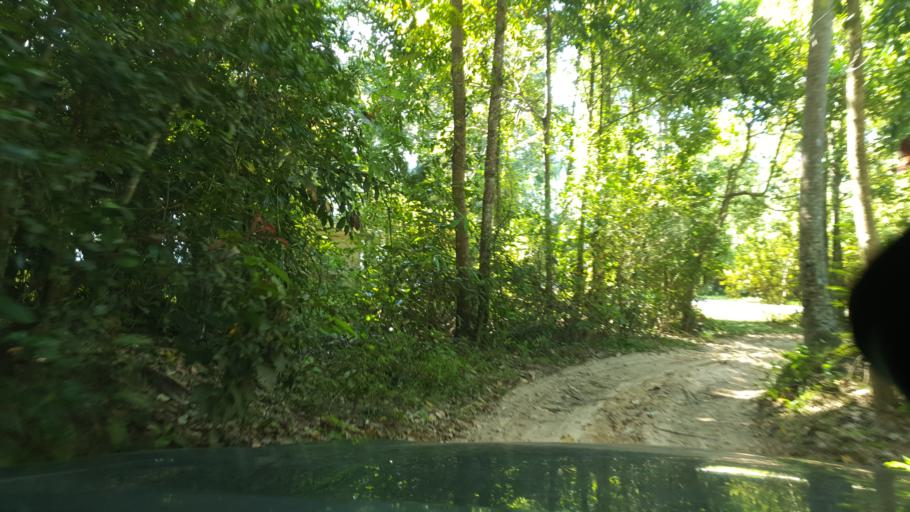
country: TH
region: Krabi
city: Krabi
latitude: 8.0220
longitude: 98.8807
